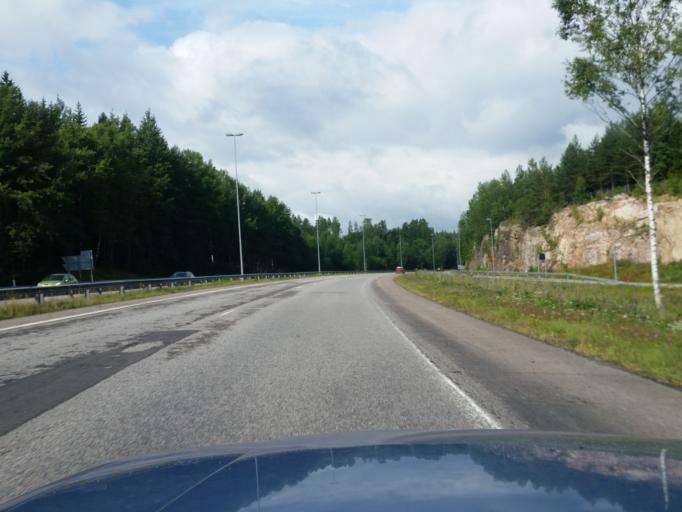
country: FI
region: Uusimaa
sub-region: Helsinki
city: Vihti
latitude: 60.2933
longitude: 24.3647
